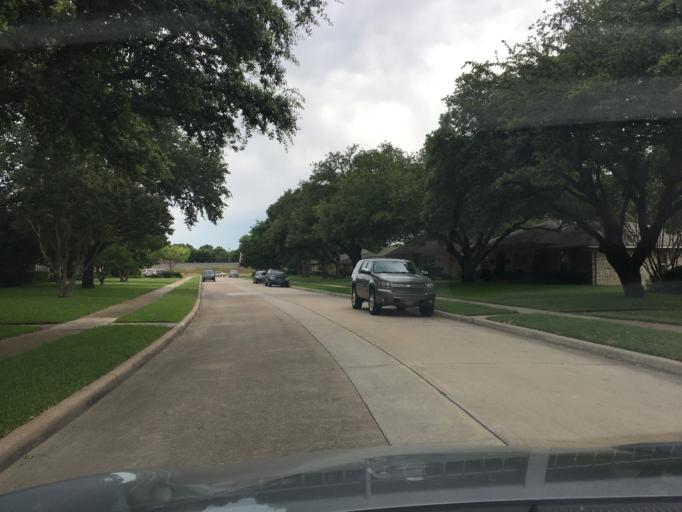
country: US
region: Texas
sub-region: Dallas County
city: Richardson
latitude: 32.9427
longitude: -96.7123
